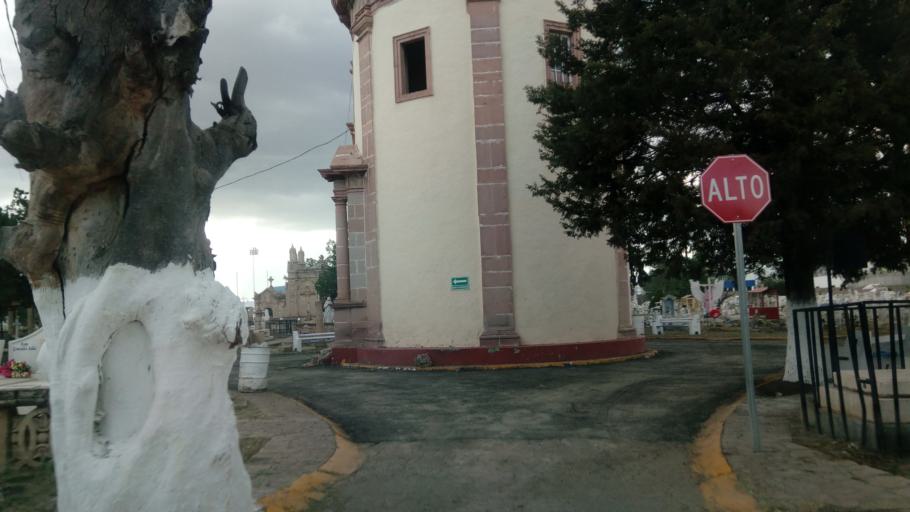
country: MX
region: Durango
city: Victoria de Durango
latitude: 24.0278
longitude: -104.6411
